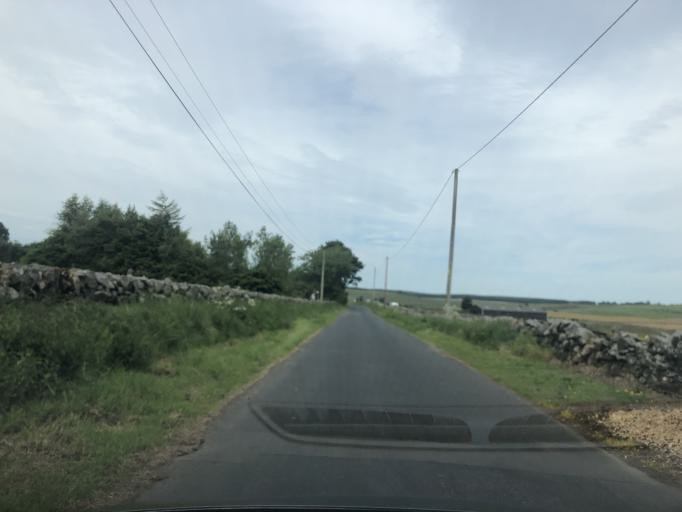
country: GB
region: Scotland
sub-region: The Scottish Borders
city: West Linton
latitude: 55.7561
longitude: -3.3462
